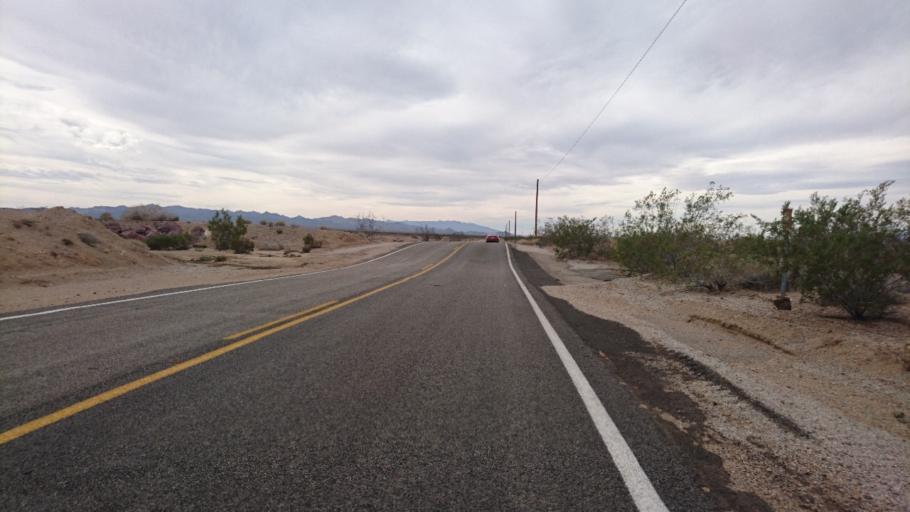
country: US
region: California
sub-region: San Bernardino County
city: Needles
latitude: 34.8906
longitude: -115.0970
